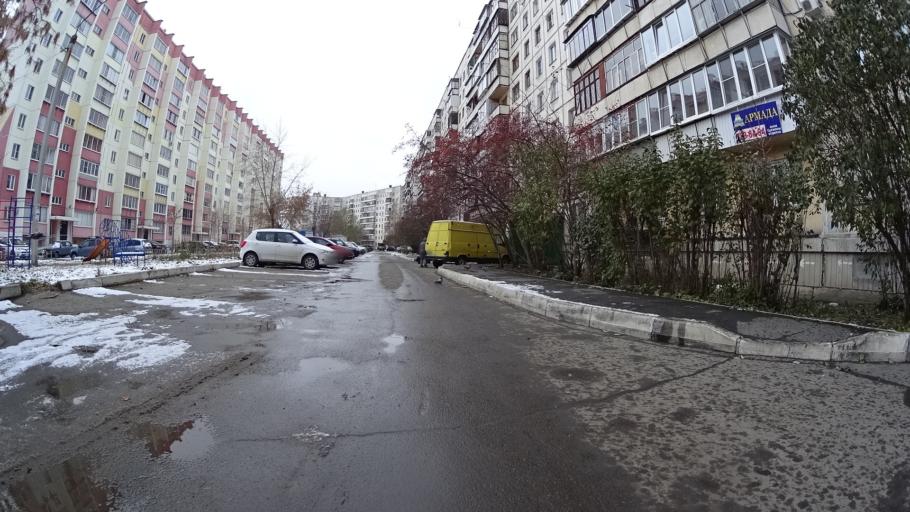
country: RU
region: Chelyabinsk
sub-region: Gorod Chelyabinsk
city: Chelyabinsk
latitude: 55.1884
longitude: 61.3263
